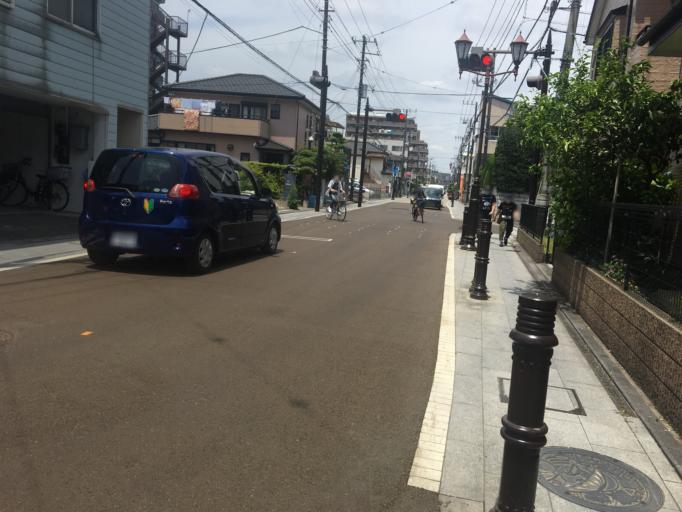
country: JP
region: Saitama
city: Shimotoda
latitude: 35.8217
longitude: 139.6813
